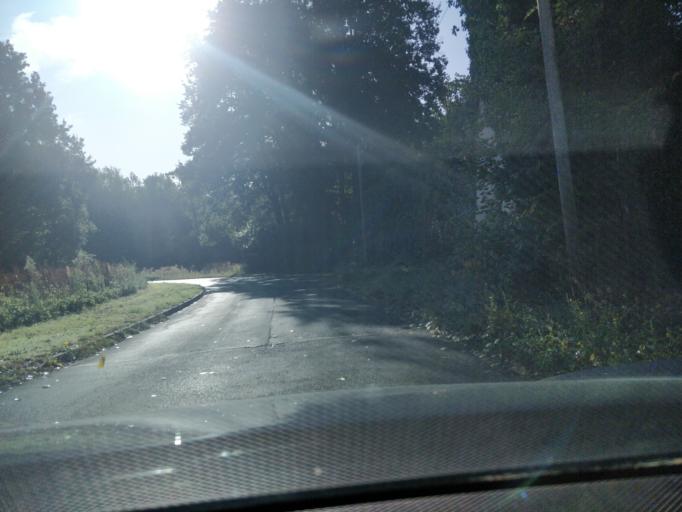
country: FR
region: Ile-de-France
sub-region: Departement de l'Essonne
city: Vaugrigneuse
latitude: 48.6024
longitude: 2.1000
